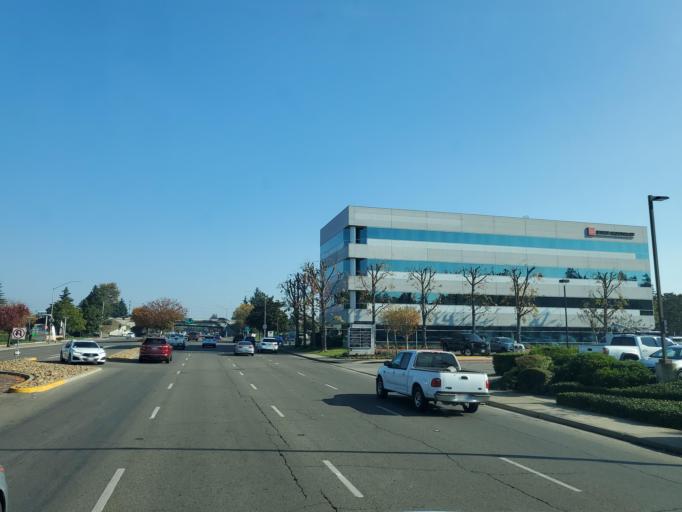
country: US
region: California
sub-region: San Joaquin County
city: Country Club
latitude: 37.9843
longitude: -121.3463
